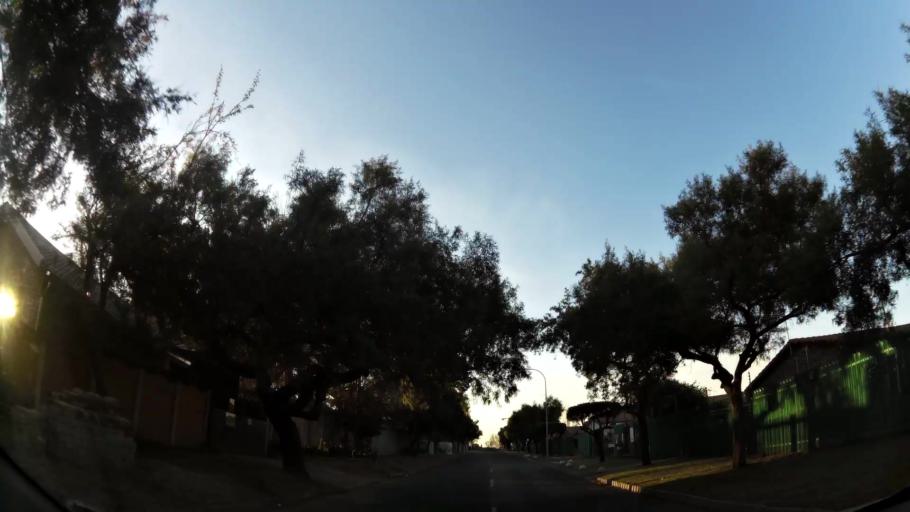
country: ZA
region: Gauteng
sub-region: City of Johannesburg Metropolitan Municipality
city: Roodepoort
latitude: -26.1498
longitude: 27.8872
